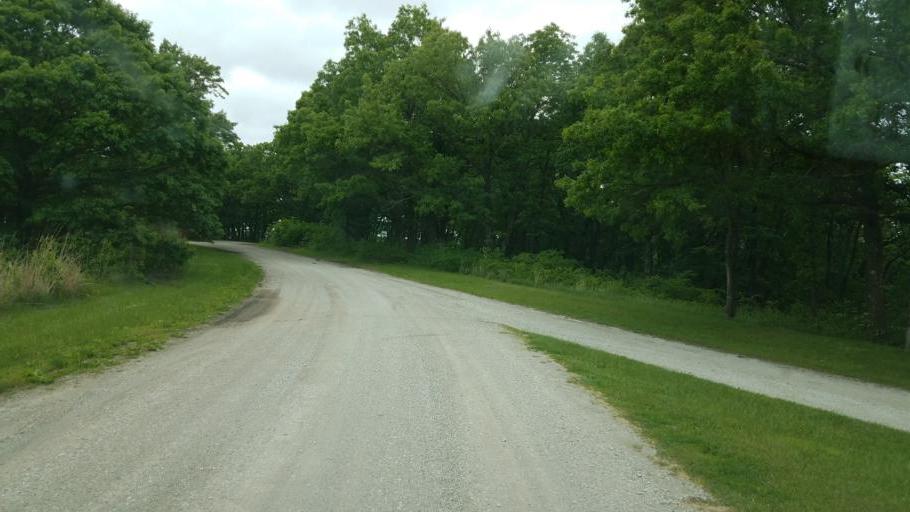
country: US
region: Iowa
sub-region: Decatur County
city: Lamoni
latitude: 40.6529
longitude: -93.8433
